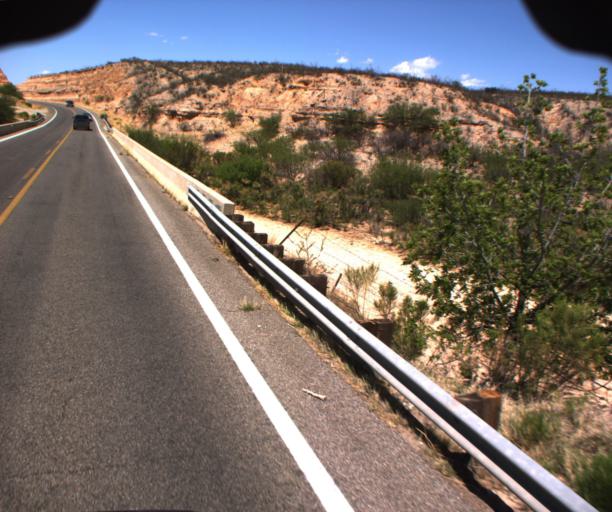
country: US
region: Arizona
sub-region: Cochise County
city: Saint David
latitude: 31.8143
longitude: -110.1657
